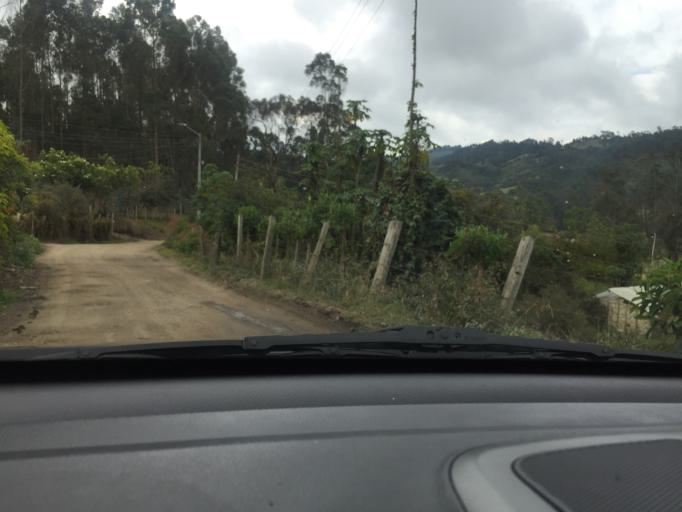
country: CO
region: Cundinamarca
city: Zipacon
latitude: 4.7613
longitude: -74.3769
